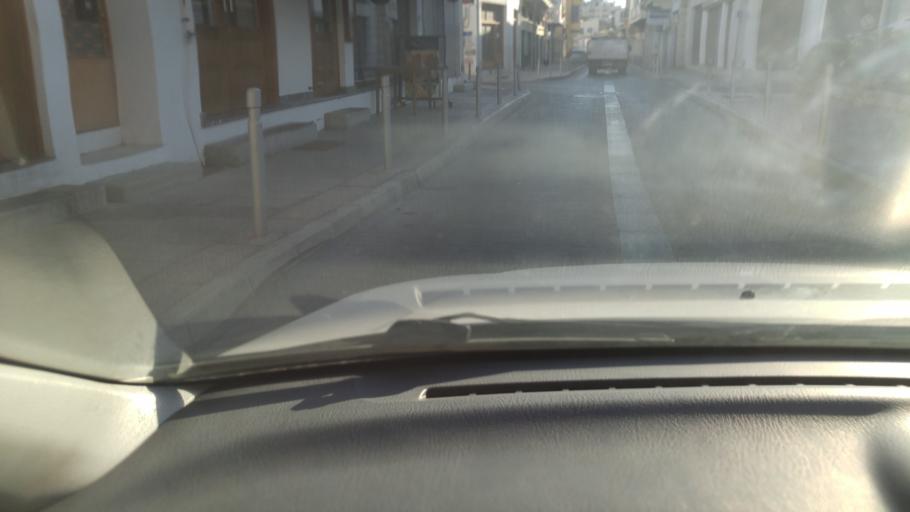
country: CY
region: Limassol
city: Limassol
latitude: 34.6725
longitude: 33.0396
